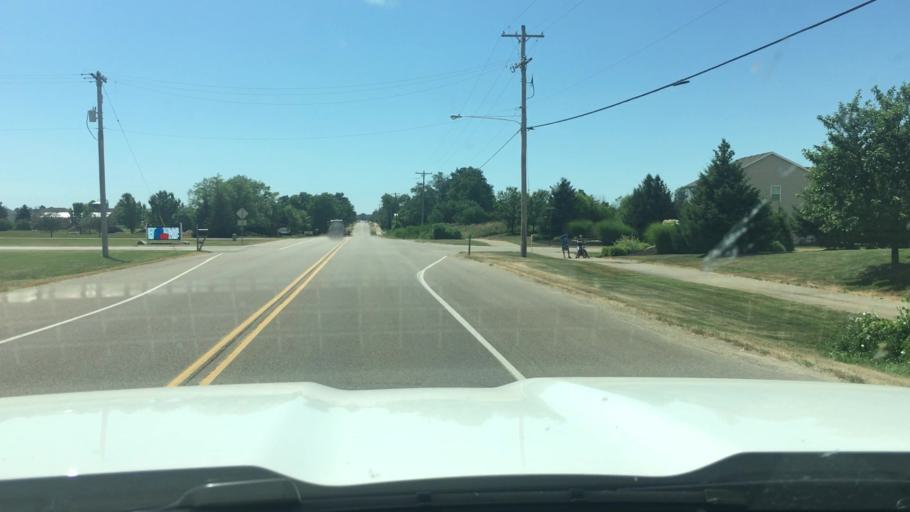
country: US
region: Michigan
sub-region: Ottawa County
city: Hudsonville
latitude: 42.8403
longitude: -85.8430
